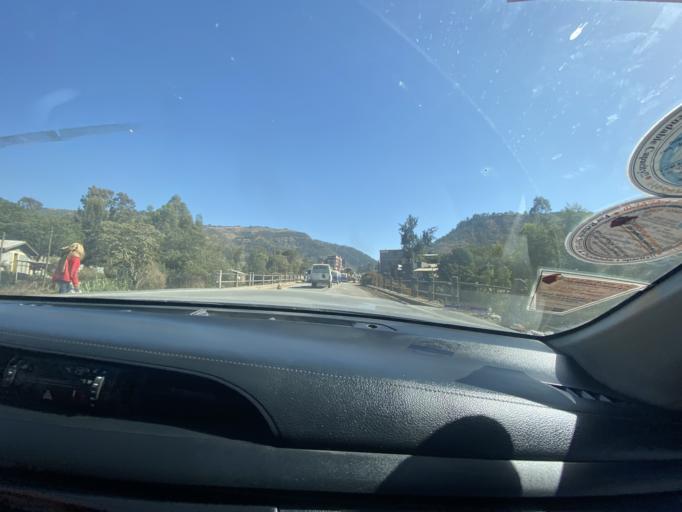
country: ET
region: Amhara
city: Robit
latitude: 11.8287
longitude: 39.5977
